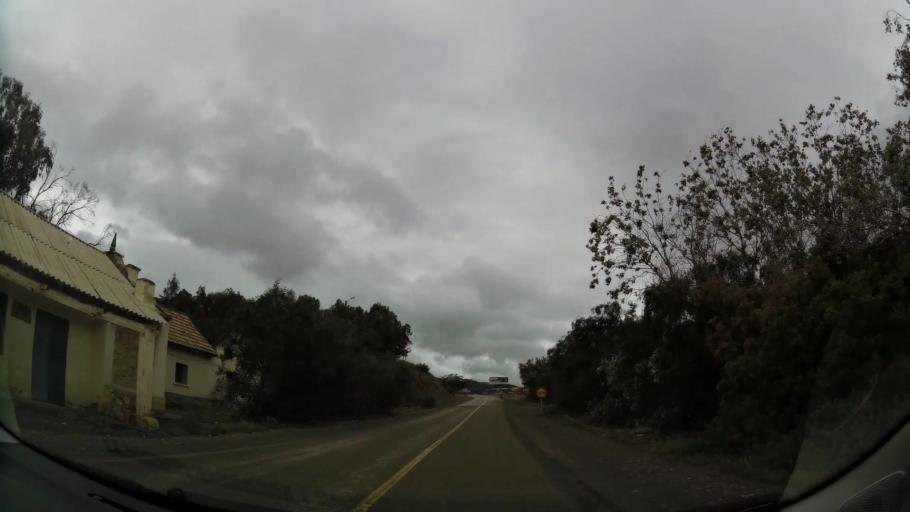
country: MA
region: Taza-Al Hoceima-Taounate
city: Imzourene
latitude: 34.9636
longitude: -3.8124
